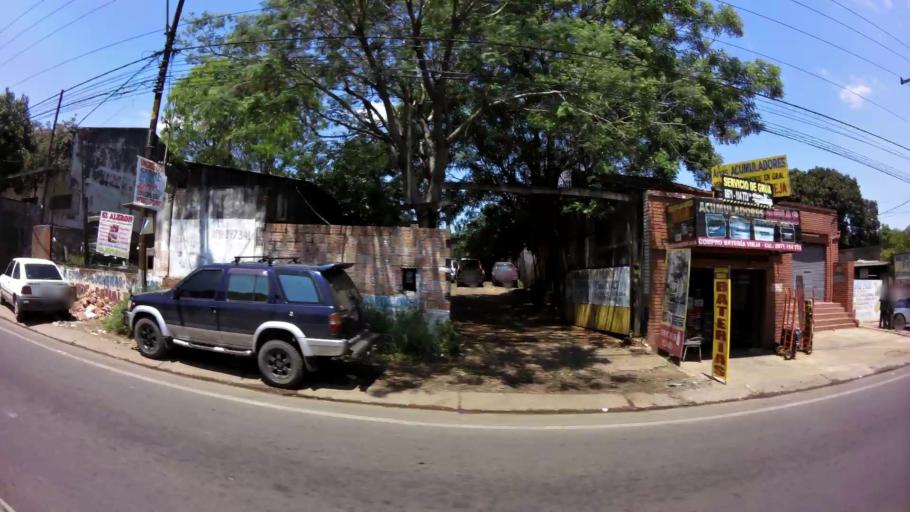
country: PY
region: Central
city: Lambare
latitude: -25.3345
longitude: -57.5787
